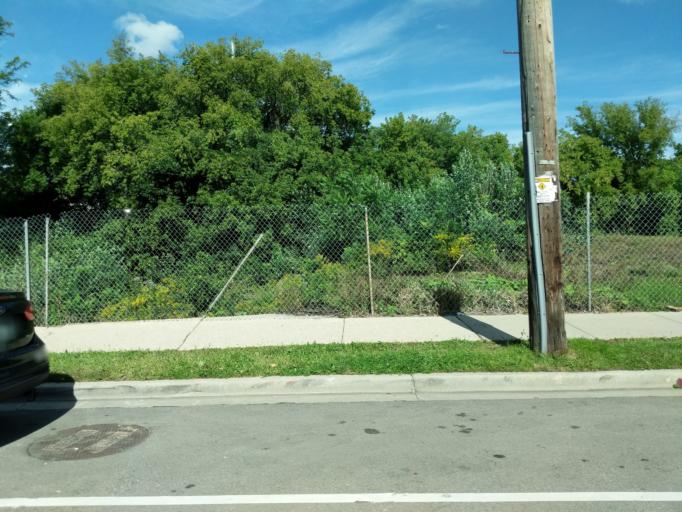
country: US
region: Wisconsin
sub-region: Milwaukee County
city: Milwaukee
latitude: 43.0529
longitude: -87.9048
